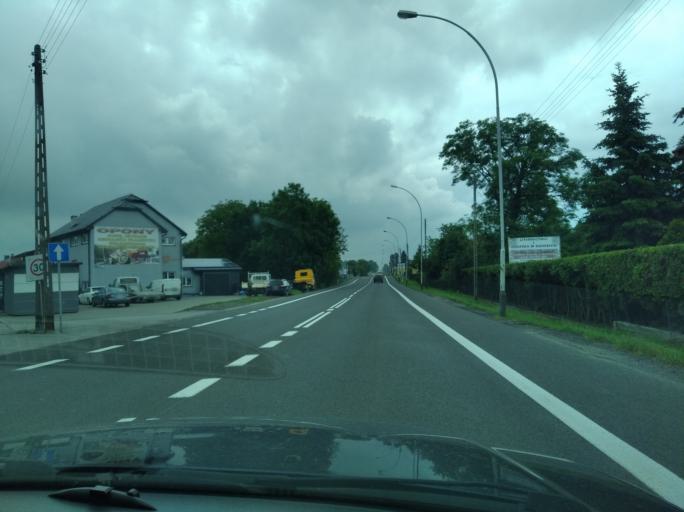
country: PL
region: Subcarpathian Voivodeship
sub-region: Powiat przeworski
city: Przeworsk
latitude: 50.0571
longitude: 22.5028
